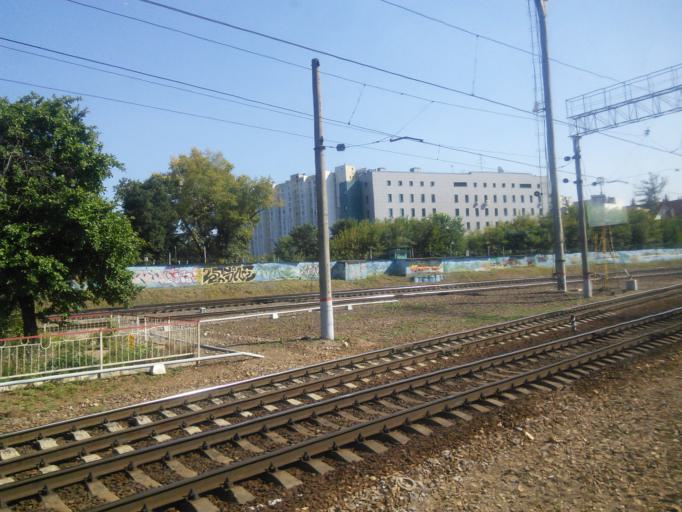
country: RU
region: Moscow
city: Tekstil'shchiki
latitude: 55.6879
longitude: 37.7350
